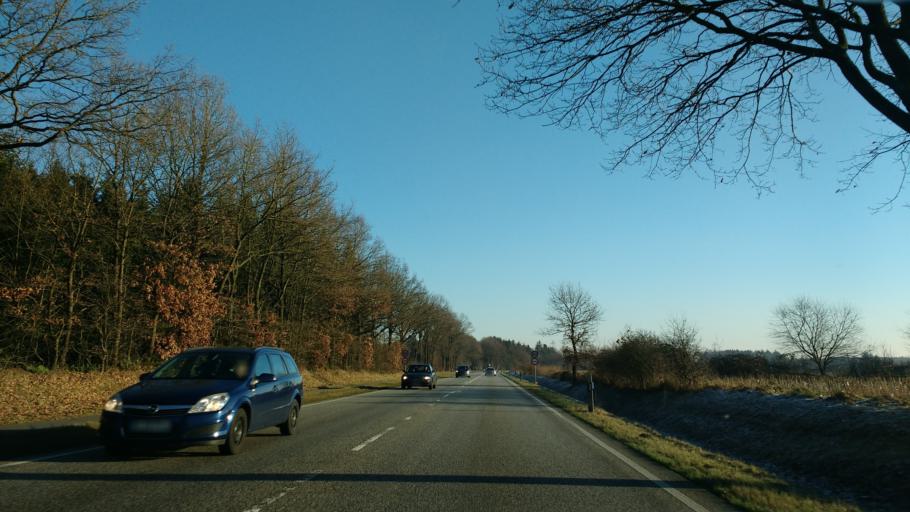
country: DE
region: Schleswig-Holstein
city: Aukrug
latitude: 54.0714
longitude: 9.8274
